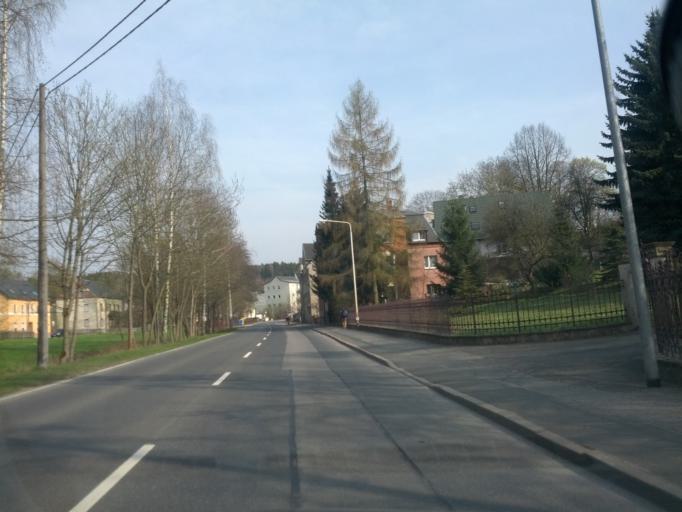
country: DE
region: Saxony
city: Kirchberg
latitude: 50.6167
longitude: 12.5346
